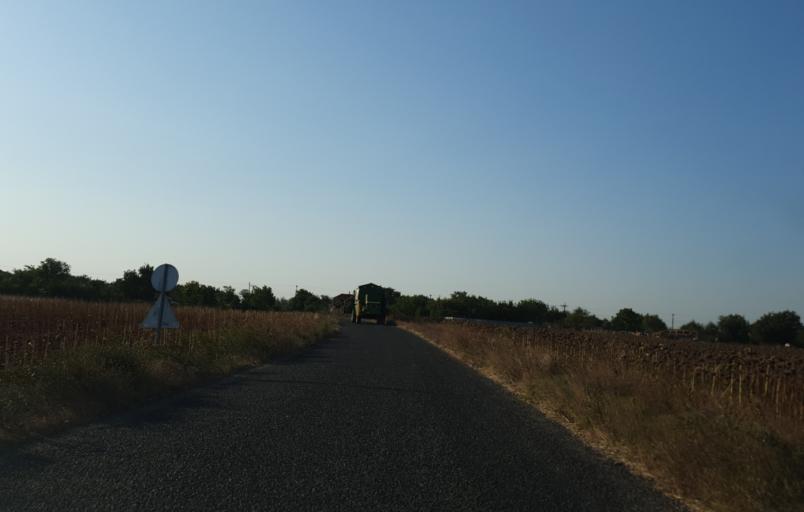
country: TR
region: Tekirdag
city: Beyazkoy
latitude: 41.4308
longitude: 27.7566
